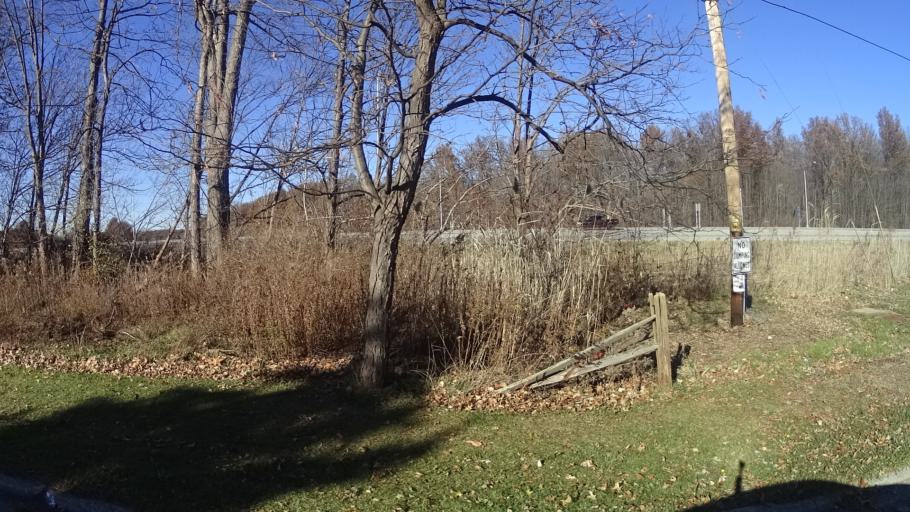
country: US
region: Ohio
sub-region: Lorain County
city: Elyria
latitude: 41.3993
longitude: -82.1560
